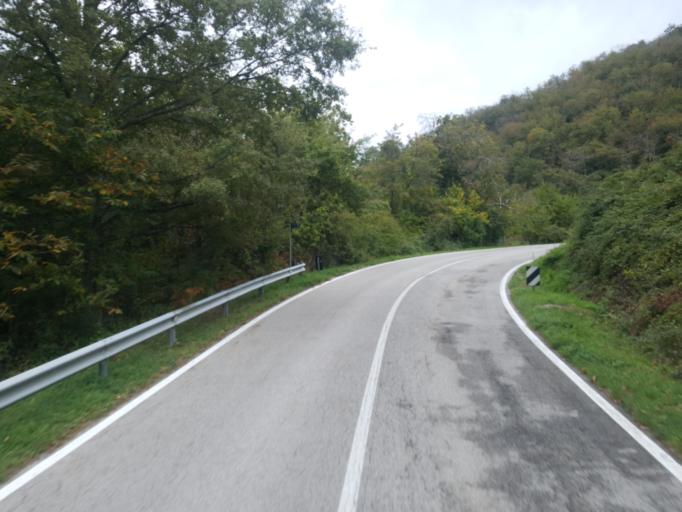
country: IT
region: Tuscany
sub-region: Province of Pisa
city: Castelnuovo di Val di Cecina
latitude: 43.2016
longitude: 10.9051
